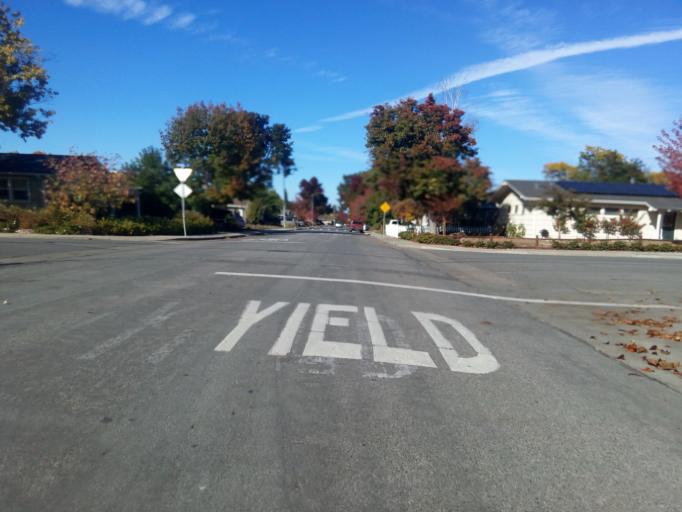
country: US
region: California
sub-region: Santa Clara County
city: Mountain View
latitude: 37.3770
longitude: -122.0795
